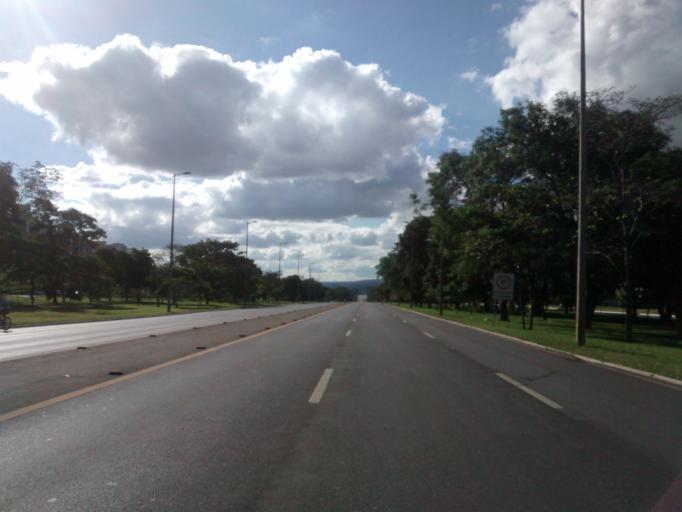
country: BR
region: Federal District
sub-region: Brasilia
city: Brasilia
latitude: -15.7619
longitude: -47.8841
